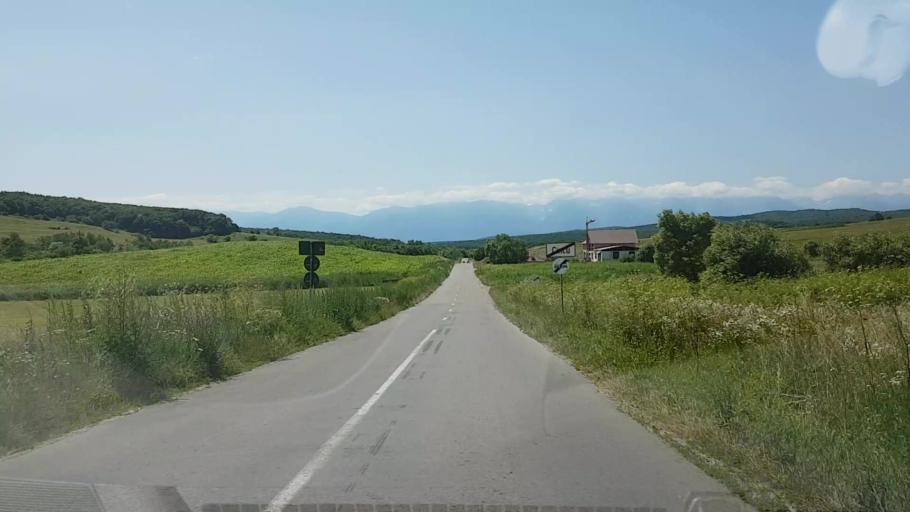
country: RO
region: Brasov
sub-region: Comuna Cincu
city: Cincu
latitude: 45.9060
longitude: 24.8116
